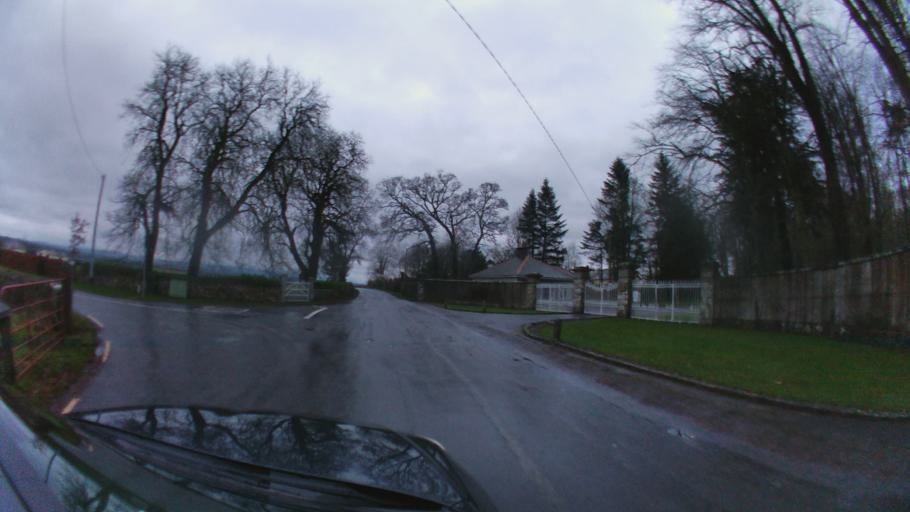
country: IE
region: Leinster
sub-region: Kilkenny
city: Graiguenamanagh
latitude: 52.6042
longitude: -6.9915
